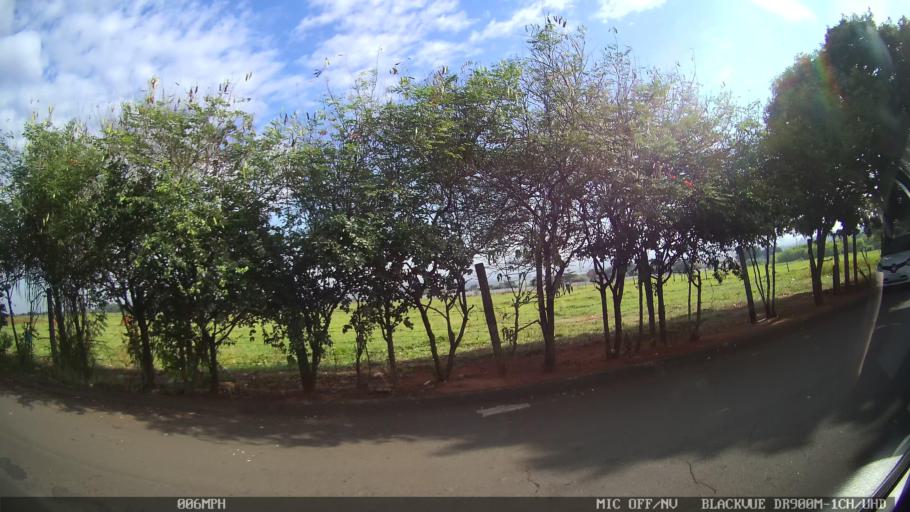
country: BR
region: Sao Paulo
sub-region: Americana
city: Americana
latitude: -22.7203
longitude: -47.3698
